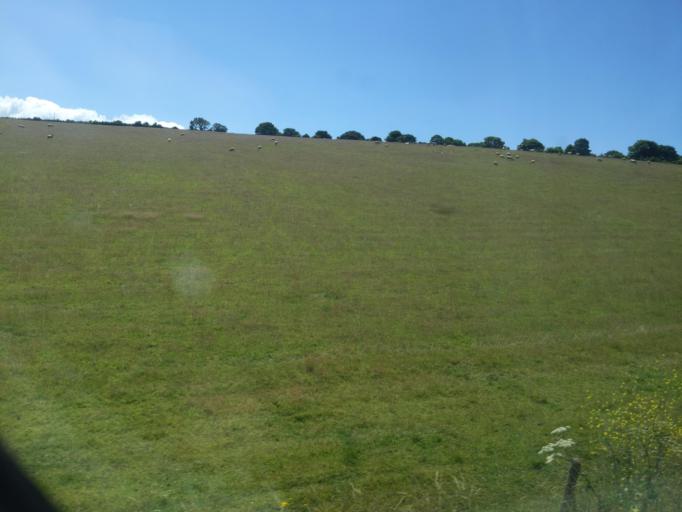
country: GB
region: England
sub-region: Cornwall
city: Saint Stephen
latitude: 50.3286
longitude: -4.8700
